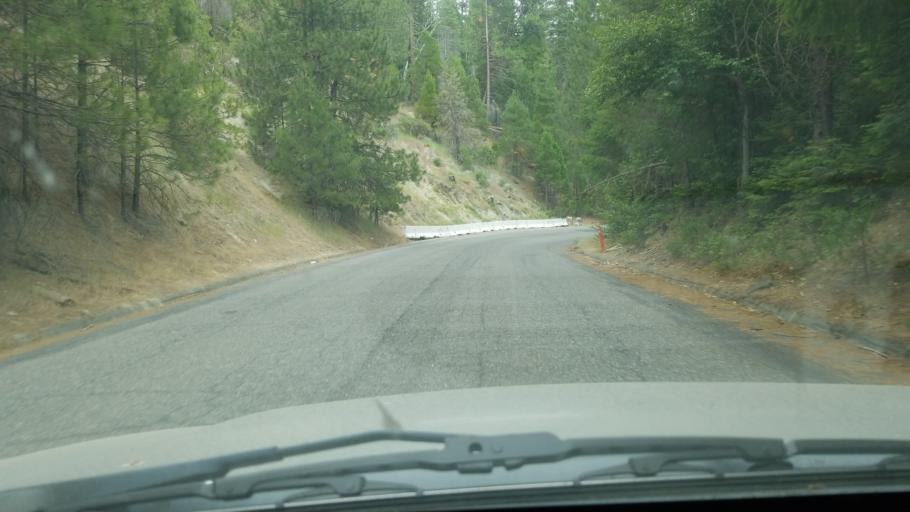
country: US
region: California
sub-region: Mariposa County
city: Midpines
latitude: 37.8151
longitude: -119.8623
